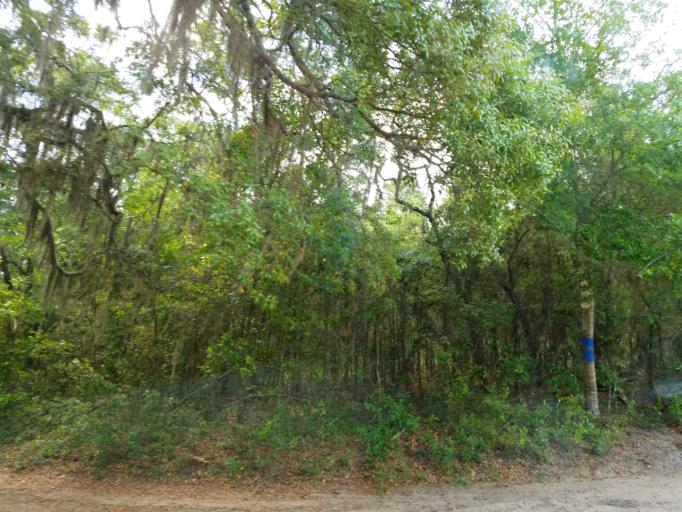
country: US
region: Florida
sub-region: Hernando County
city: Hill 'n Dale
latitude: 28.5502
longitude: -82.2723
